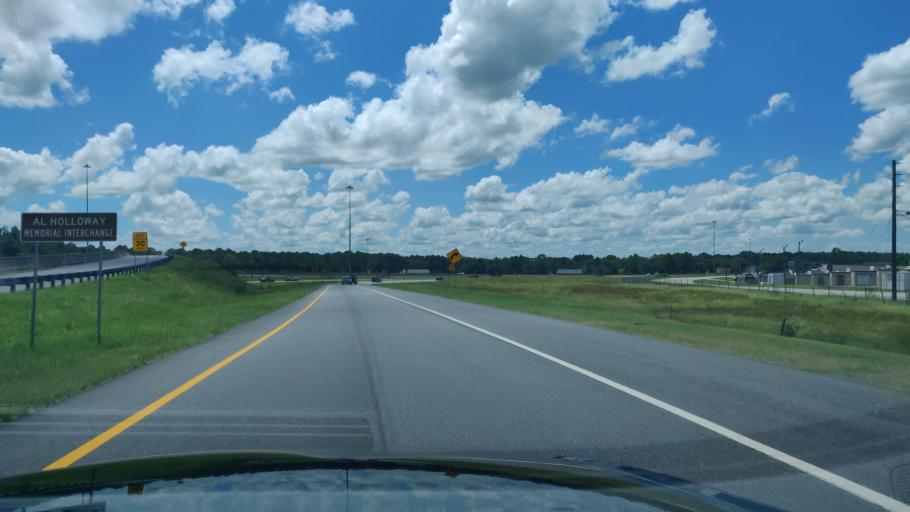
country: US
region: Georgia
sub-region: Dougherty County
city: Albany
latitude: 31.6231
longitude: -84.2281
